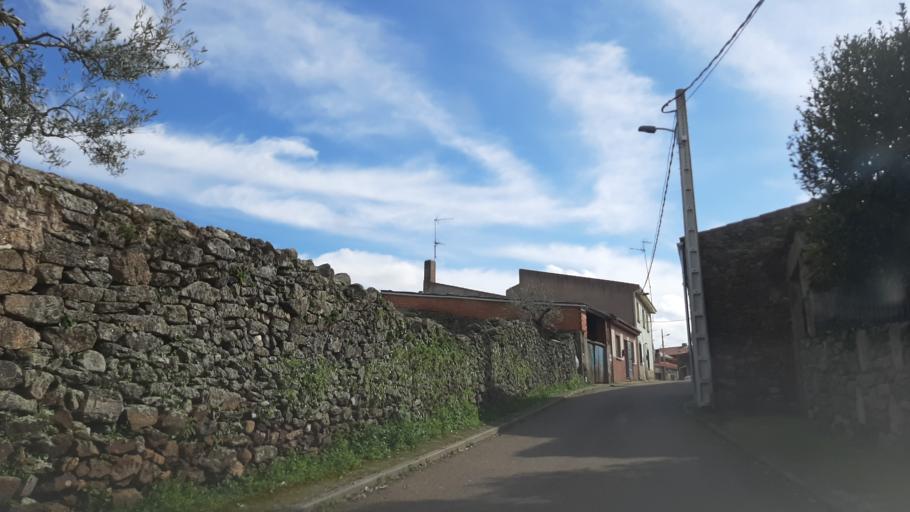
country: ES
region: Castille and Leon
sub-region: Provincia de Salamanca
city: Villarino de los Aires
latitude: 41.2423
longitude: -6.5235
